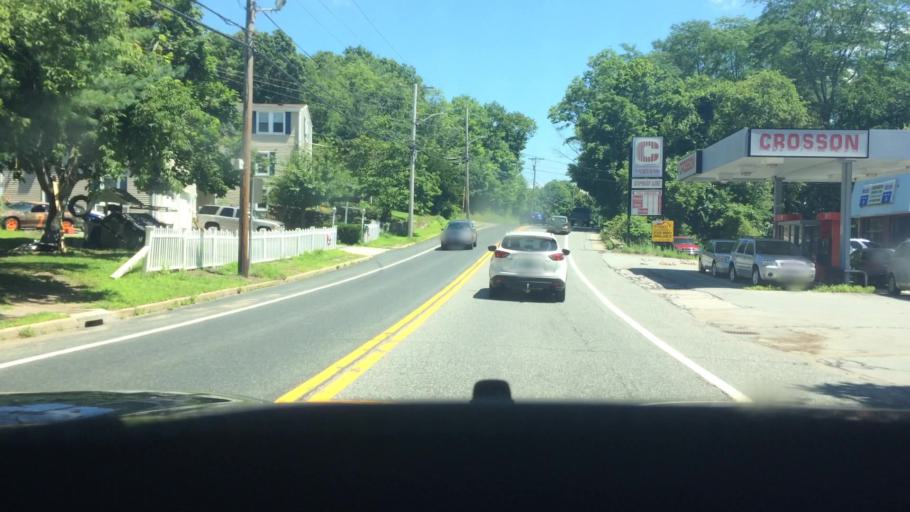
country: US
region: Massachusetts
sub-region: Worcester County
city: Blackstone
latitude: 41.9972
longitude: -71.5455
